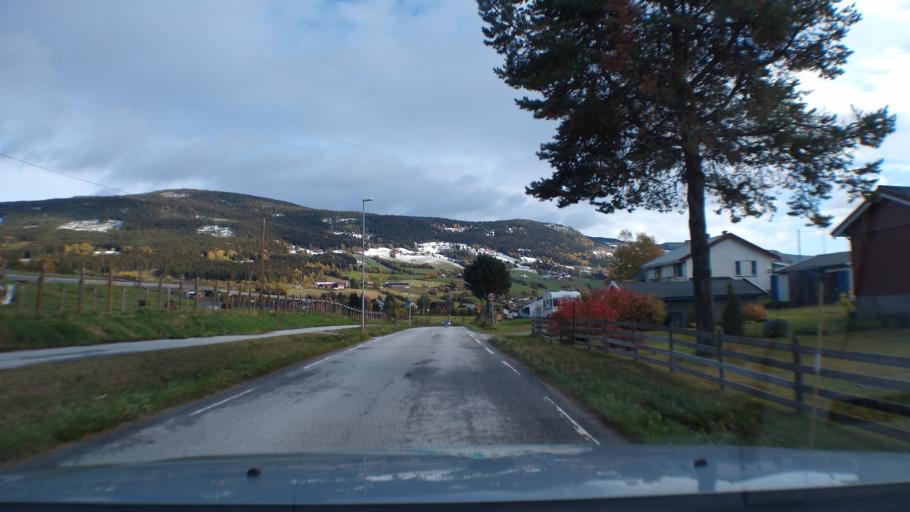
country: NO
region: Oppland
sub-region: Ringebu
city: Ringebu
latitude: 61.5366
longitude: 10.1300
